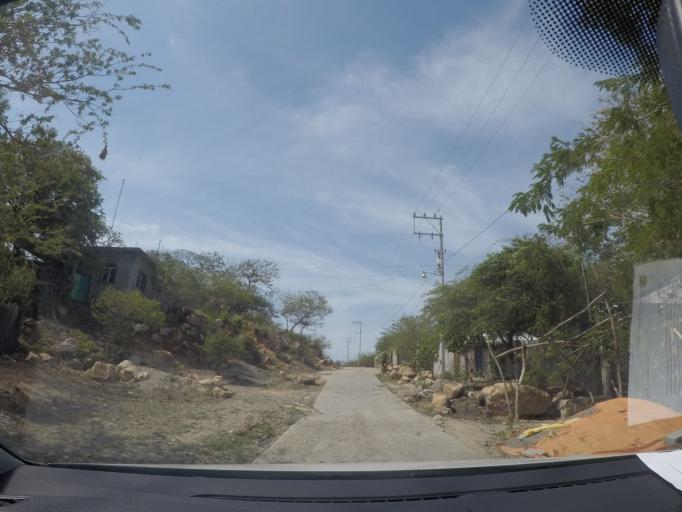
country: MX
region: Oaxaca
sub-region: Salina Cruz
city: Salina Cruz
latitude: 16.2174
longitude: -95.1258
